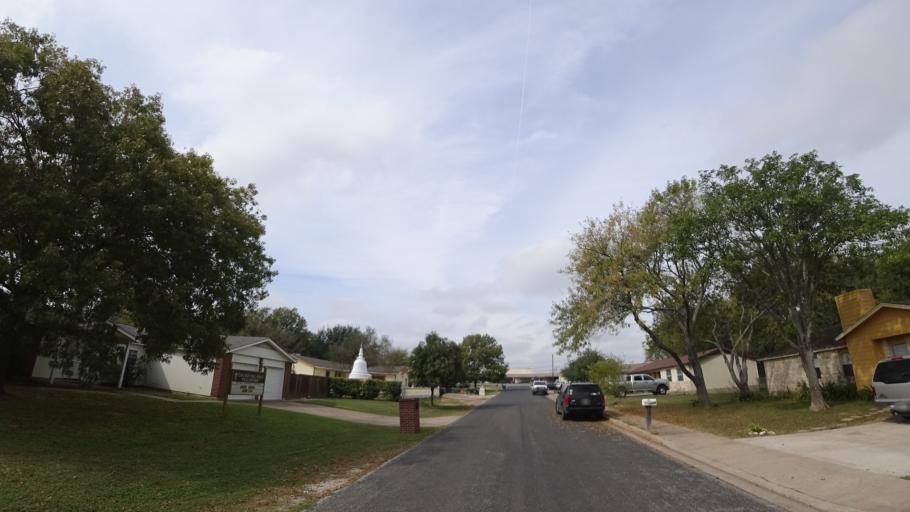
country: US
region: Texas
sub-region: Travis County
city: Wells Branch
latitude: 30.4452
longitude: -97.6622
